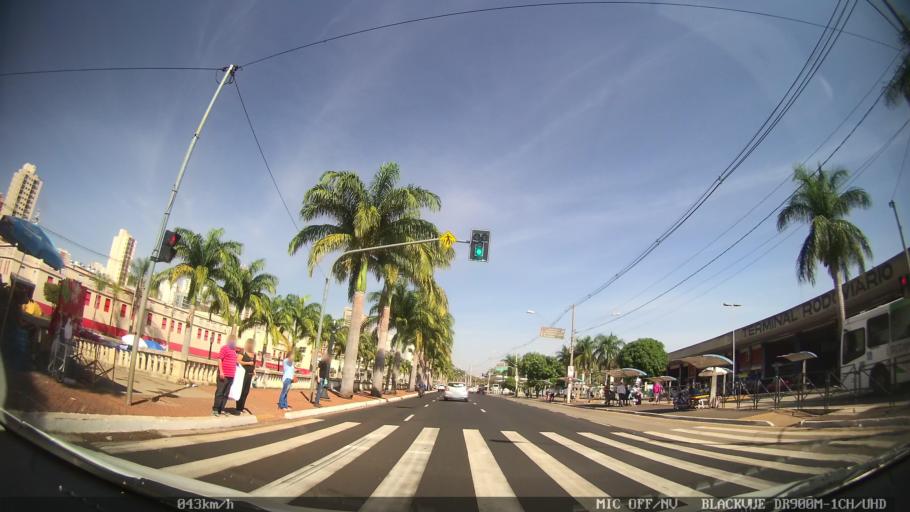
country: BR
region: Sao Paulo
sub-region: Ribeirao Preto
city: Ribeirao Preto
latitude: -21.1739
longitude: -47.8139
